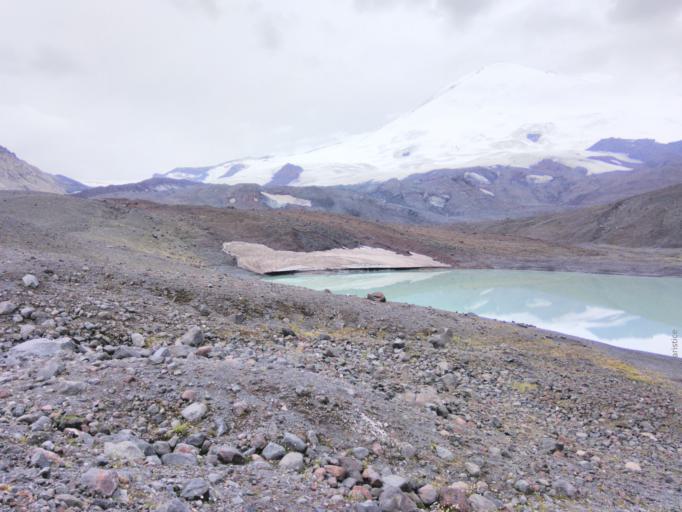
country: RU
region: Kabardino-Balkariya
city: Terskol
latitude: 43.3802
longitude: 42.5395
